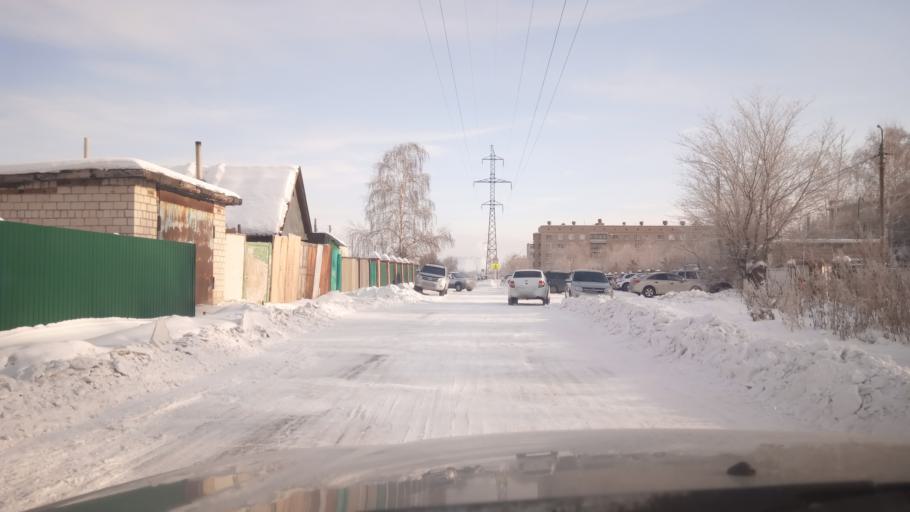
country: RU
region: Orenburg
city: Novotroitsk
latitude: 51.2115
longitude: 58.2934
